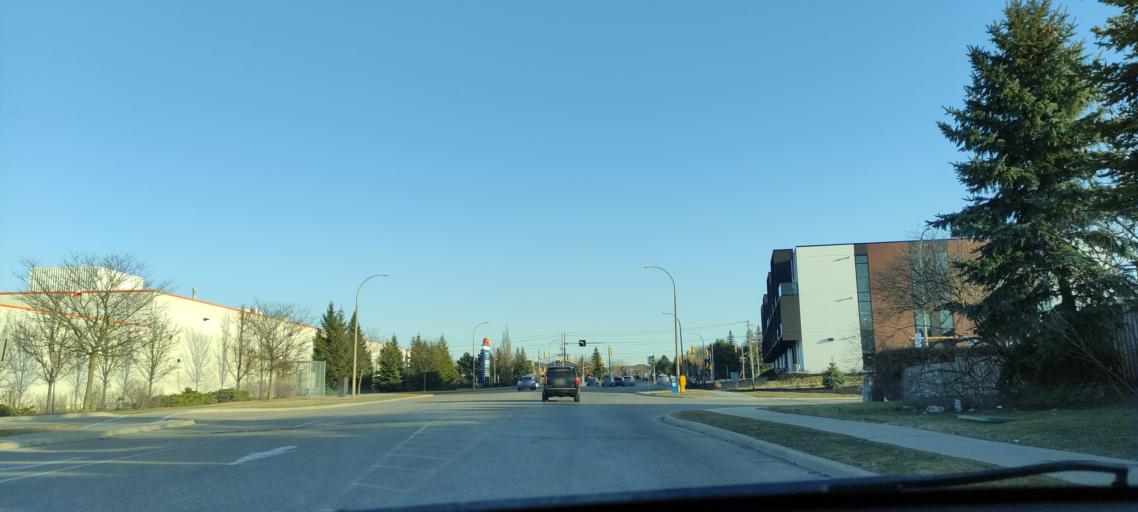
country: CA
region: Ontario
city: Kitchener
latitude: 43.4141
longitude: -80.5179
